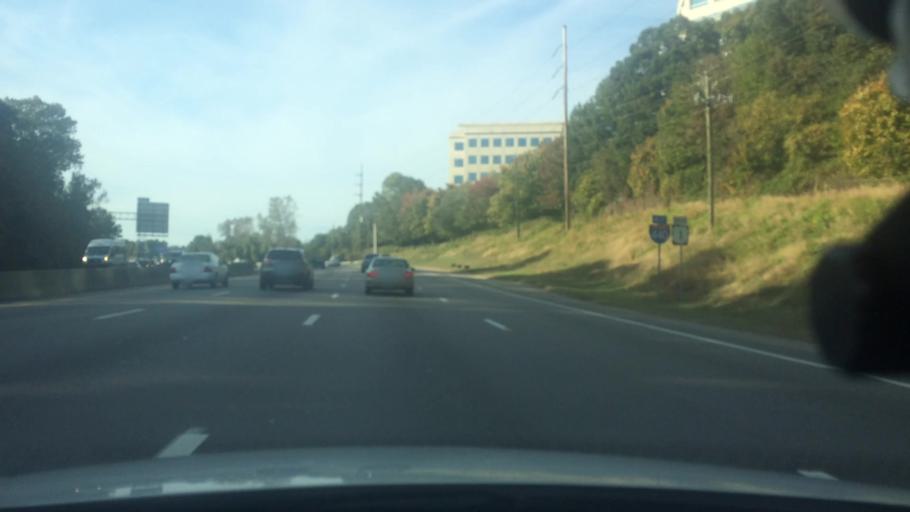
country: US
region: North Carolina
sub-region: Wake County
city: Raleigh
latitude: 35.8191
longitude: -78.6086
